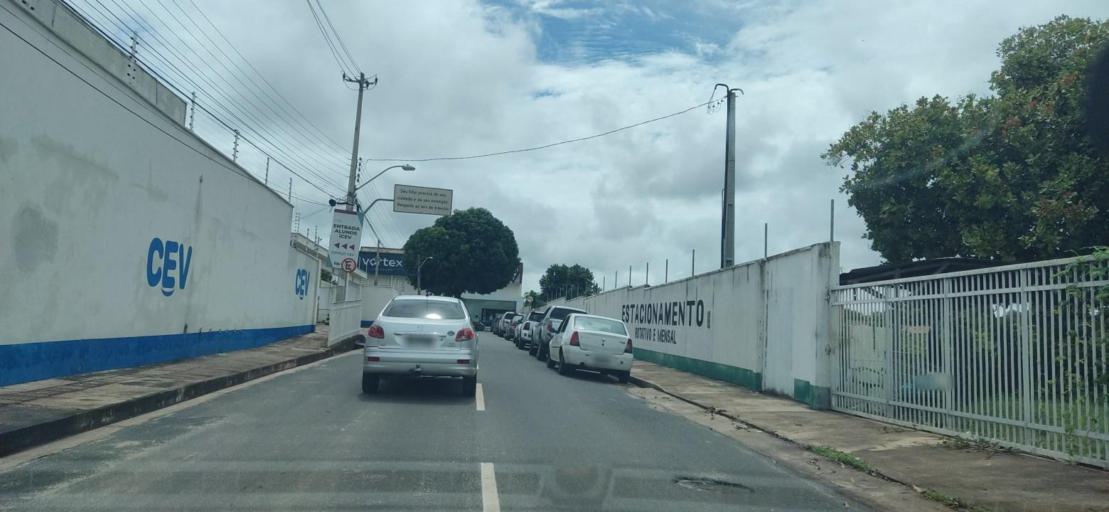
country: BR
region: Piaui
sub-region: Teresina
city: Teresina
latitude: -5.0731
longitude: -42.7711
